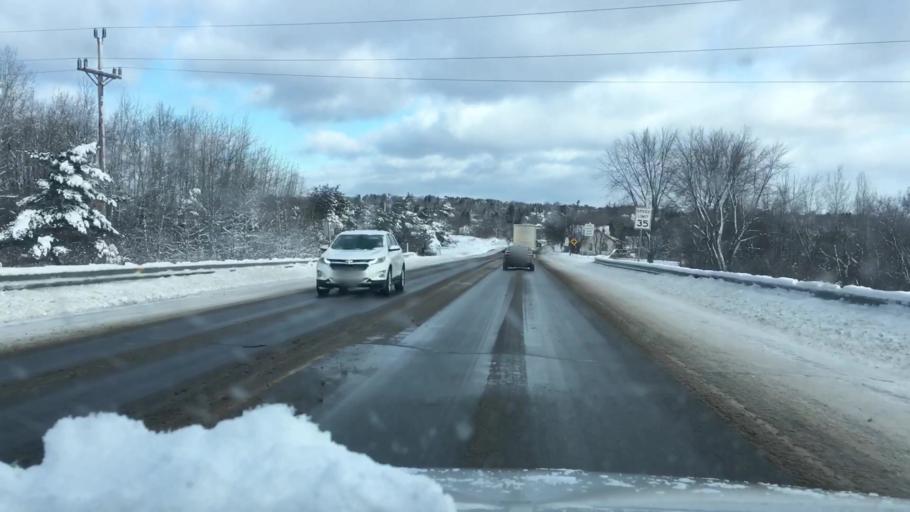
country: US
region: Maine
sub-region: Aroostook County
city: Caribou
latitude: 46.8502
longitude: -68.0050
